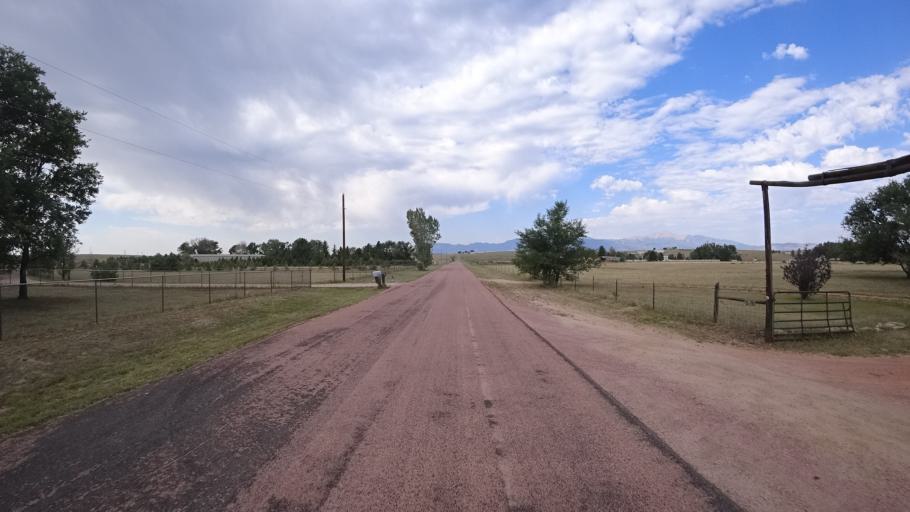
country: US
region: Colorado
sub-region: El Paso County
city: Cimarron Hills
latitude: 38.9149
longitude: -104.6697
